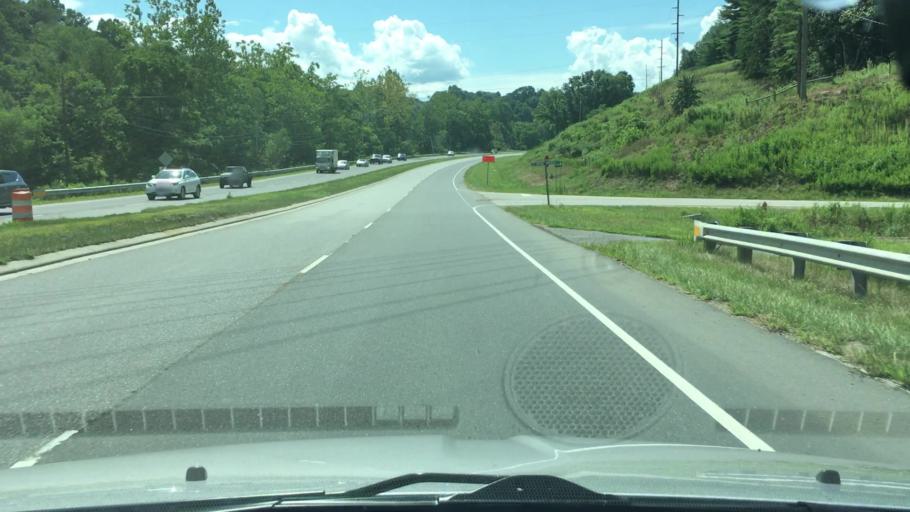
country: US
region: North Carolina
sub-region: Yancey County
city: Burnsville
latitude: 35.9108
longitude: -82.2253
